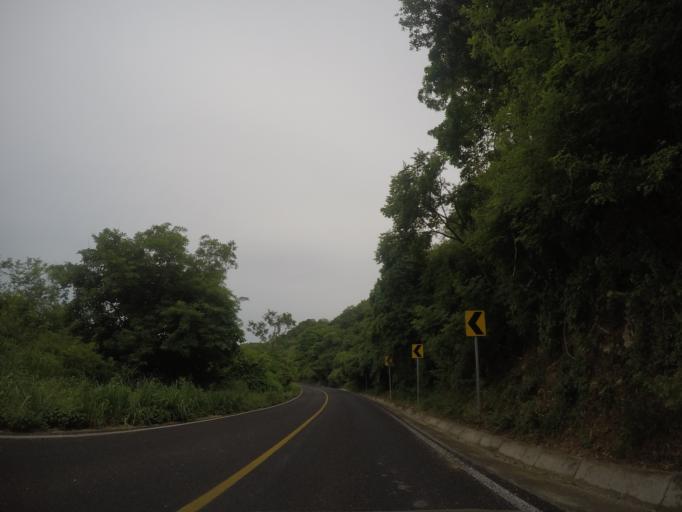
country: MX
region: Oaxaca
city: San Pedro Mixtepec
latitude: 15.9510
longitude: -97.2608
